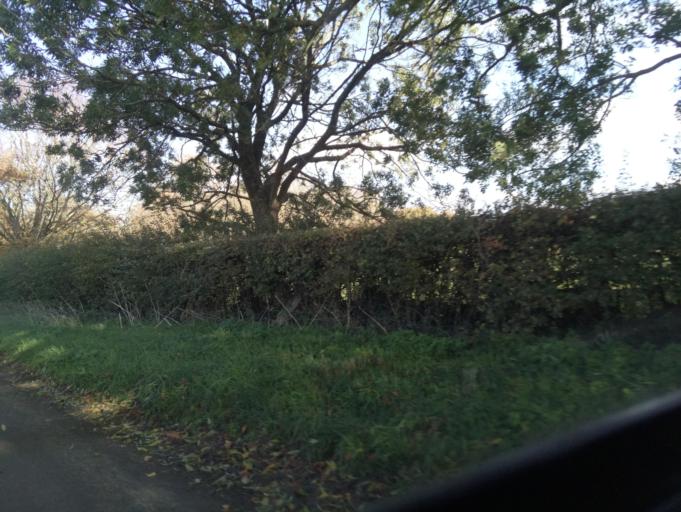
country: GB
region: England
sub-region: Somerset
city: Castle Cary
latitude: 51.0487
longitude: -2.4823
